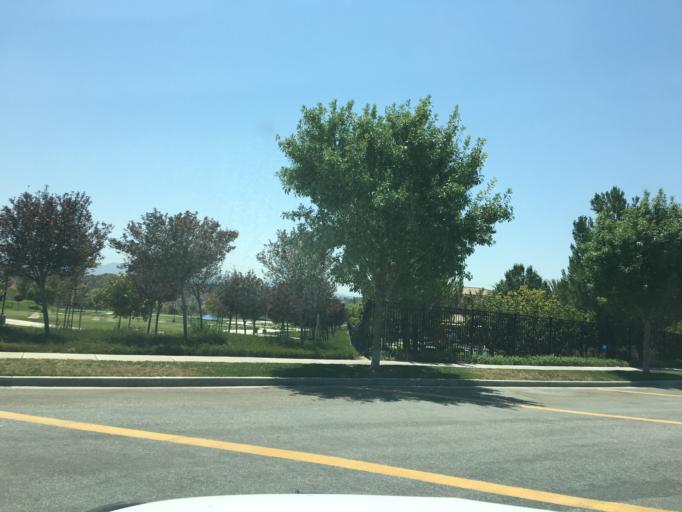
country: US
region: California
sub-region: Los Angeles County
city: Valencia
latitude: 34.4567
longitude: -118.5606
